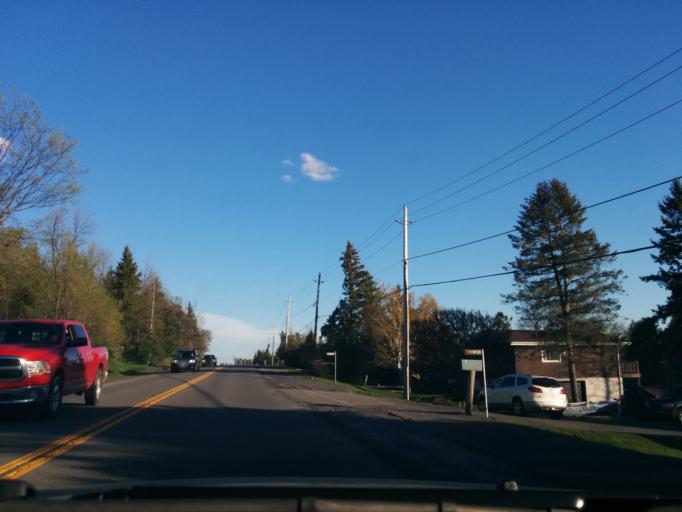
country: CA
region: Ontario
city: Bells Corners
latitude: 45.2298
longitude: -75.6705
